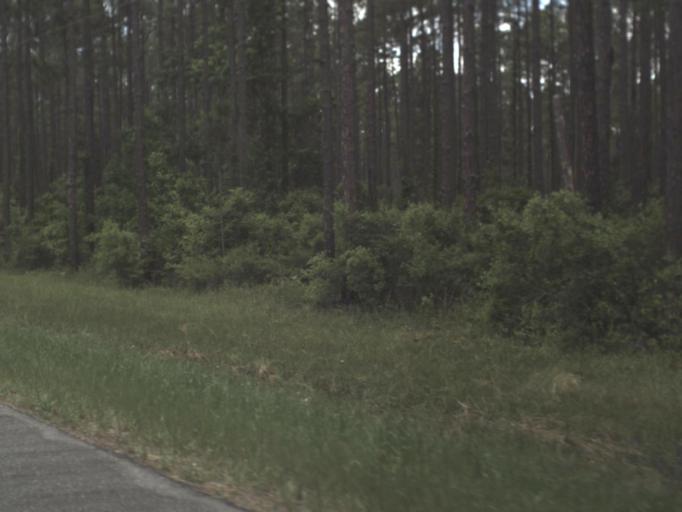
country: US
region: Florida
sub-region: Calhoun County
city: Blountstown
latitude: 30.3631
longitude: -85.1009
